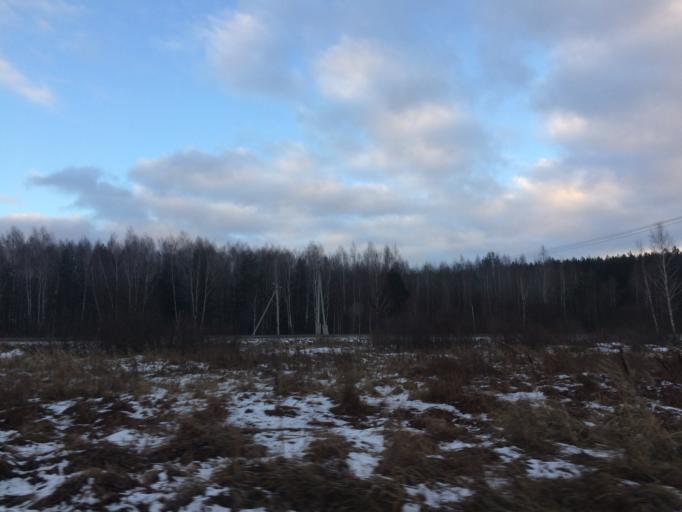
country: RU
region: Tula
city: Cherepet'
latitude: 54.1162
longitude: 36.3579
